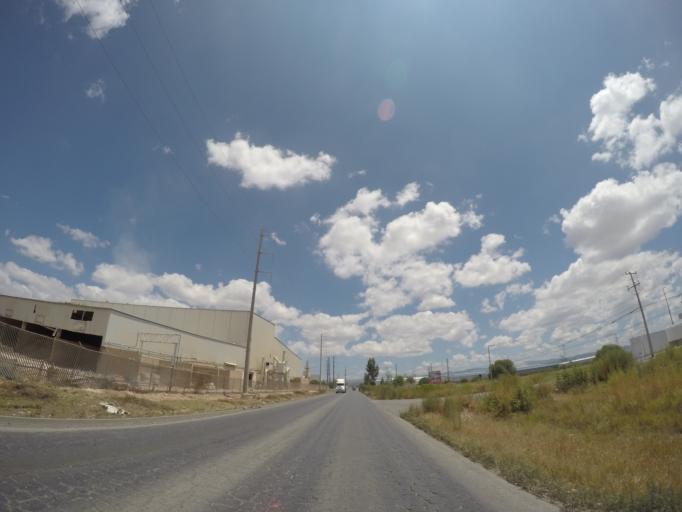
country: MX
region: San Luis Potosi
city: La Pila
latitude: 22.0481
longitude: -100.8722
